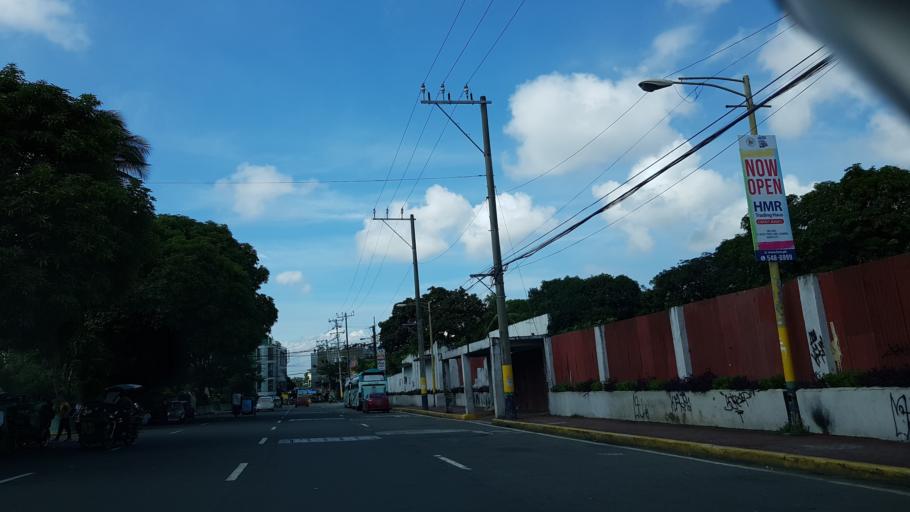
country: PH
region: Metro Manila
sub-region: Mandaluyong
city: Mandaluyong City
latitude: 14.5738
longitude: 121.0163
